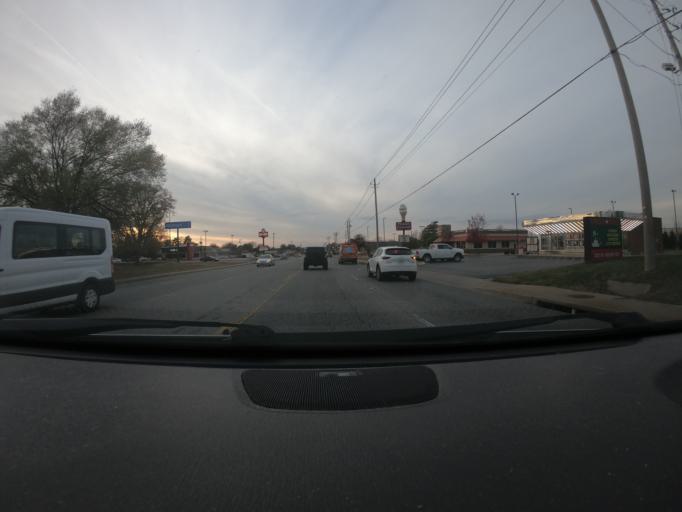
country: US
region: Arkansas
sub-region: Benton County
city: Rogers
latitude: 36.3342
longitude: -94.1486
